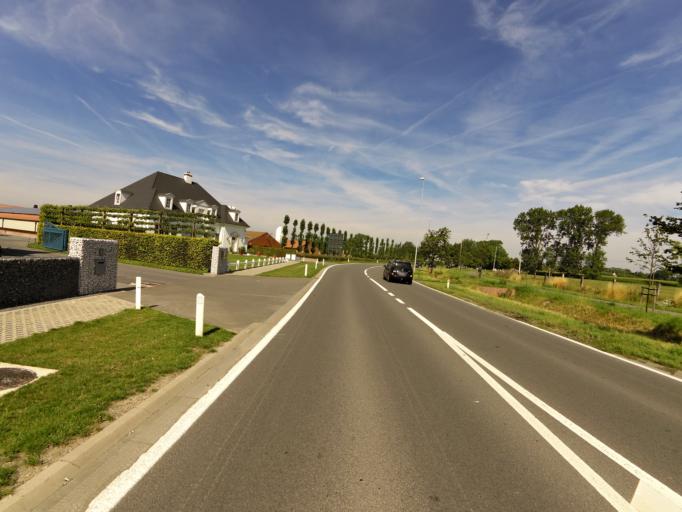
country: BE
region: Flanders
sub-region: Provincie West-Vlaanderen
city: Brugge
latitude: 51.2307
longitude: 3.1859
